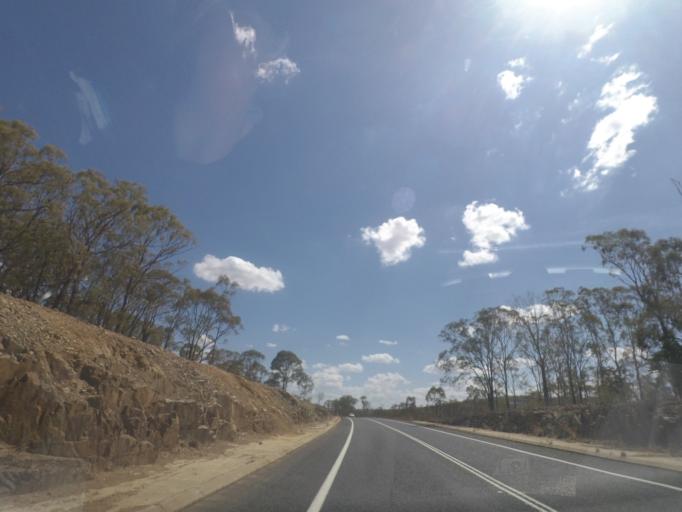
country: AU
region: Queensland
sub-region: Southern Downs
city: Warwick
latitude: -28.2196
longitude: 151.5564
